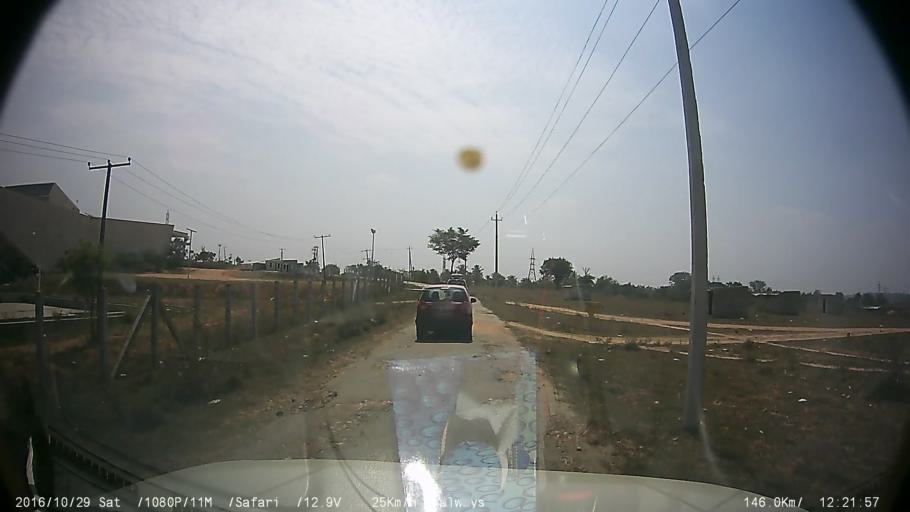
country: IN
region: Karnataka
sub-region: Mysore
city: Mysore
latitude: 12.3652
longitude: 76.5600
